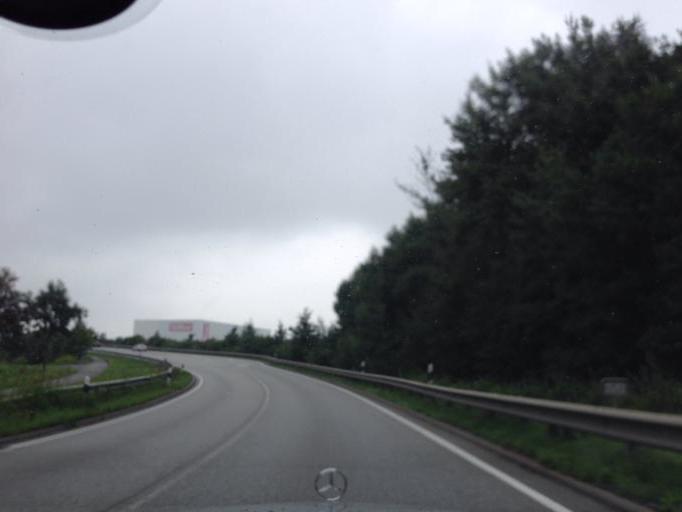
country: DE
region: Schleswig-Holstein
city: Glinde
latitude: 53.5725
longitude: 10.2014
